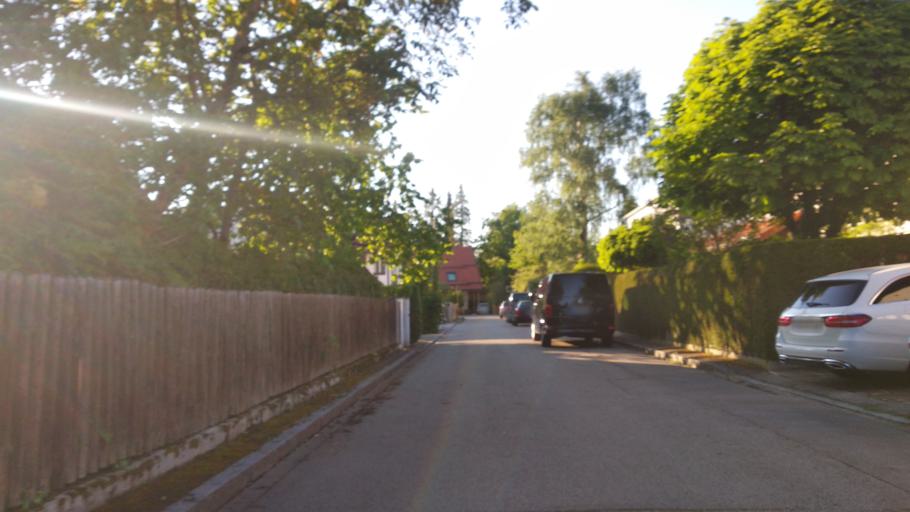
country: DE
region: Bavaria
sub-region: Upper Bavaria
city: Vaterstetten
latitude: 48.1025
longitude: 11.7788
